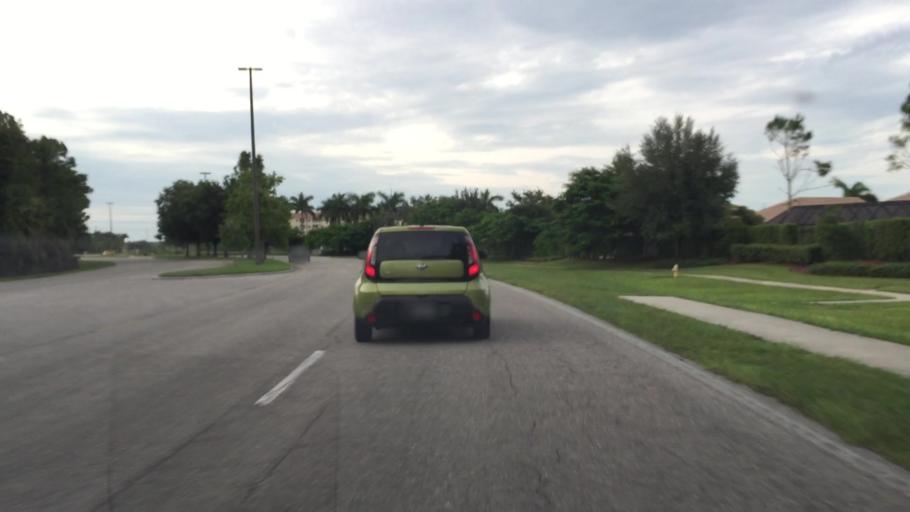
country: US
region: Florida
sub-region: Lee County
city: Fort Myers
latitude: 26.6232
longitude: -81.7930
